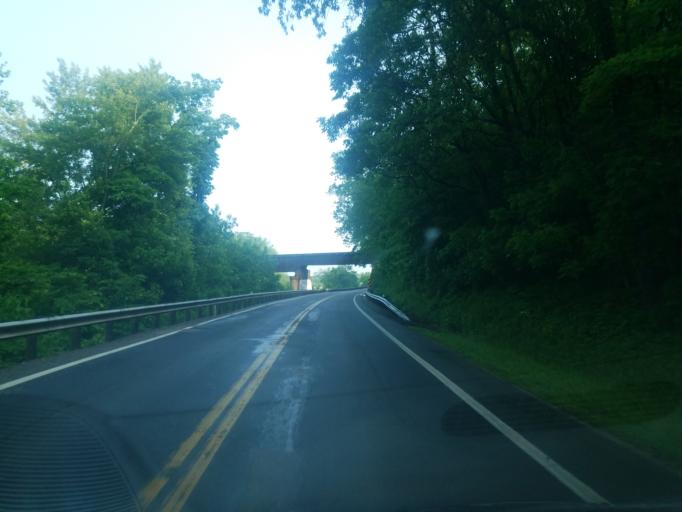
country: US
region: Ohio
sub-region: Tuscarawas County
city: Dover
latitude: 40.6020
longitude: -81.4165
